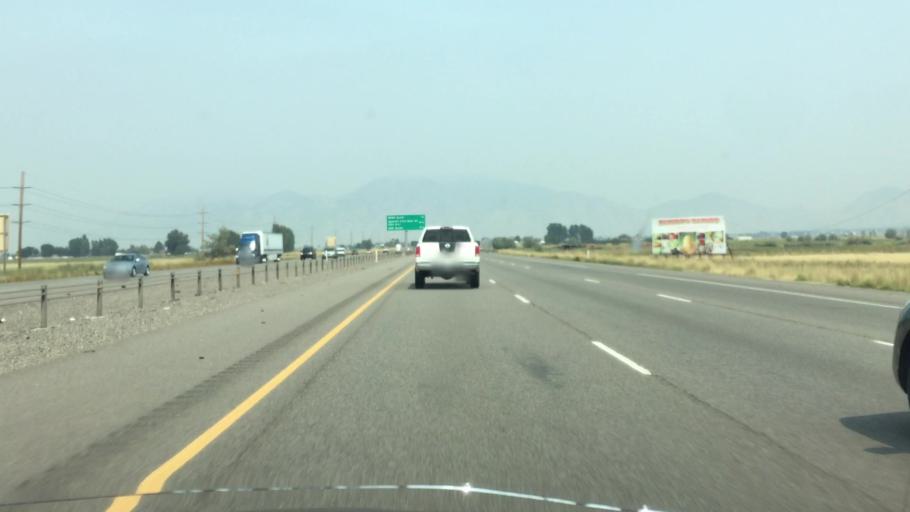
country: US
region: Utah
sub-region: Utah County
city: Payson
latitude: 40.0710
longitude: -111.7174
